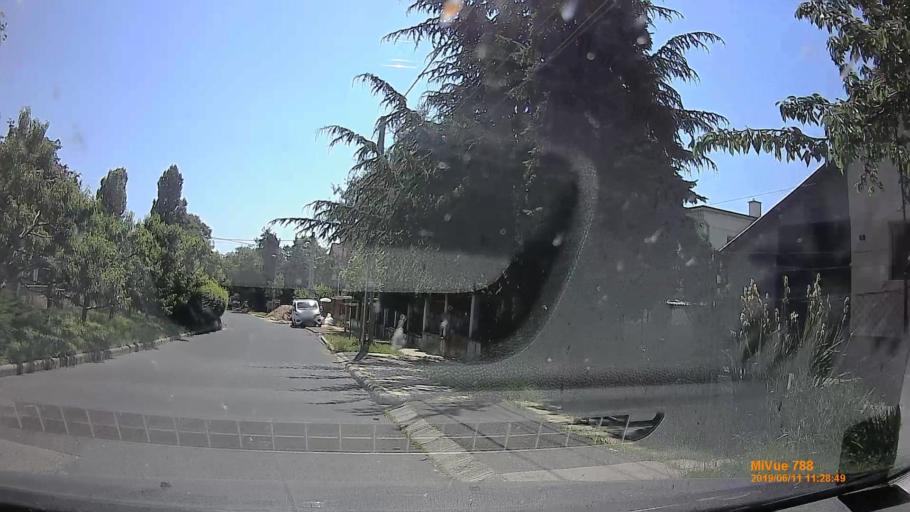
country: HU
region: Budapest
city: Budapest XXII. keruelet
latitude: 47.4414
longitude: 19.0272
